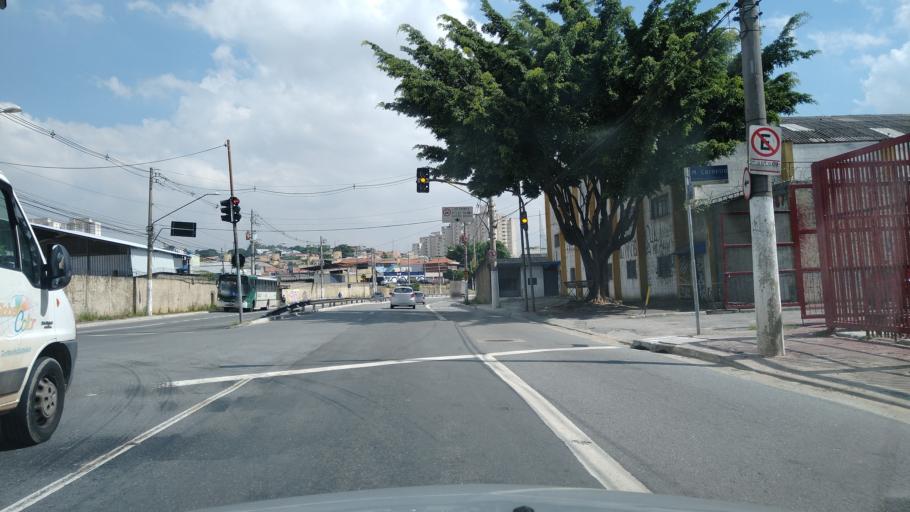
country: BR
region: Sao Paulo
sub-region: Guarulhos
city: Guarulhos
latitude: -23.4948
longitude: -46.5084
